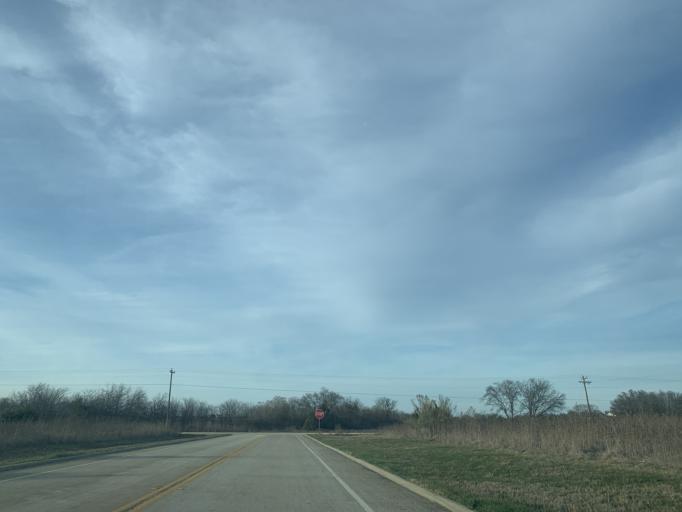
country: US
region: Texas
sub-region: Bell County
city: Salado
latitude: 30.8753
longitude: -97.5825
